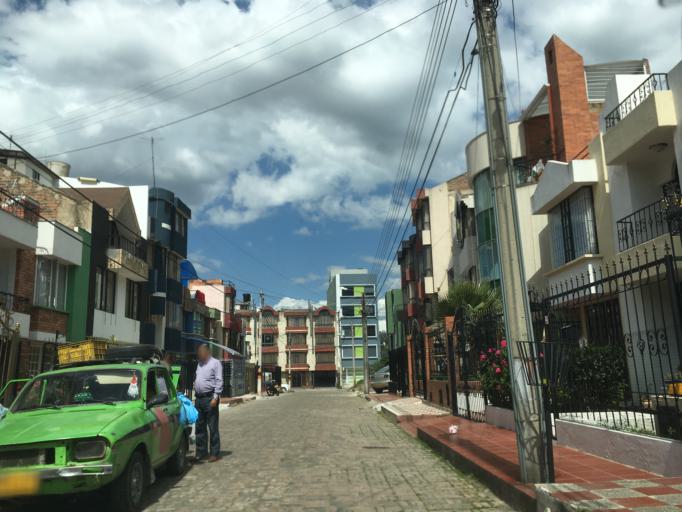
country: CO
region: Boyaca
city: Sogamoso
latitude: 5.7240
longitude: -72.9206
